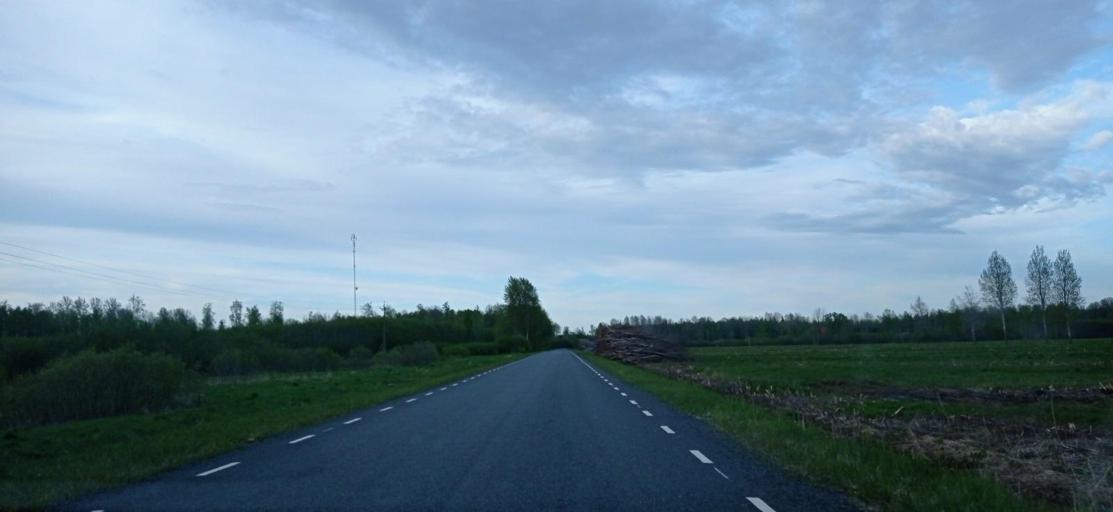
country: EE
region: Paernumaa
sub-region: Tootsi vald
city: Tootsi
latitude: 58.5623
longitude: 24.8001
